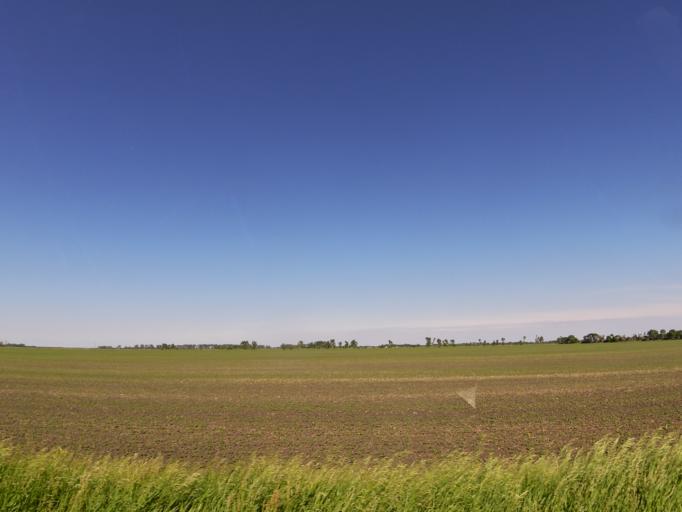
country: US
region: North Dakota
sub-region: Walsh County
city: Grafton
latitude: 48.4076
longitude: -97.2556
